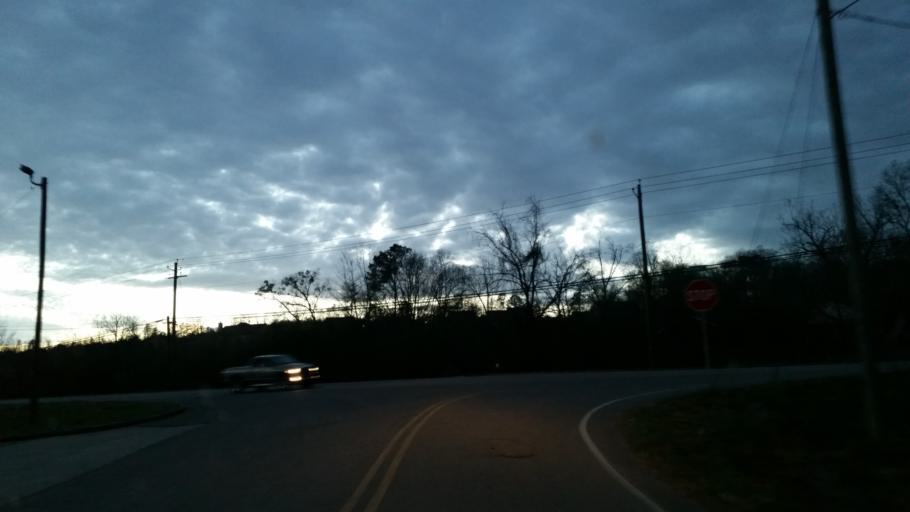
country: US
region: Georgia
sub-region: Cherokee County
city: Ball Ground
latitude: 34.3178
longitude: -84.3959
